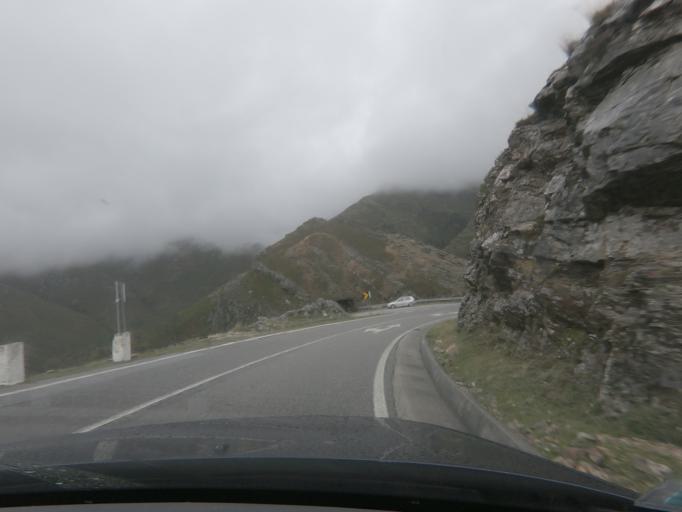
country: PT
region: Vila Real
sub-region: Mondim de Basto
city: Mondim de Basto
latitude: 41.3365
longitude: -7.8691
